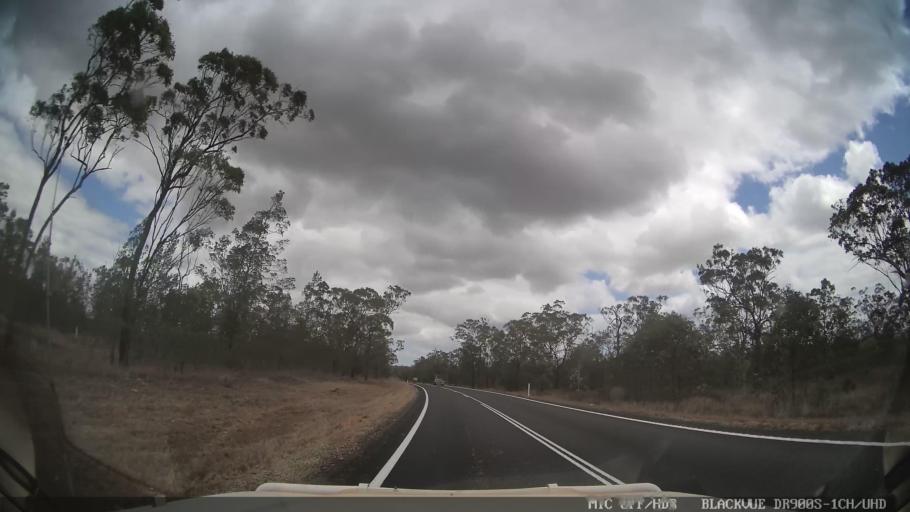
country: AU
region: Queensland
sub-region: Tablelands
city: Ravenshoe
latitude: -17.6571
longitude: 145.2483
